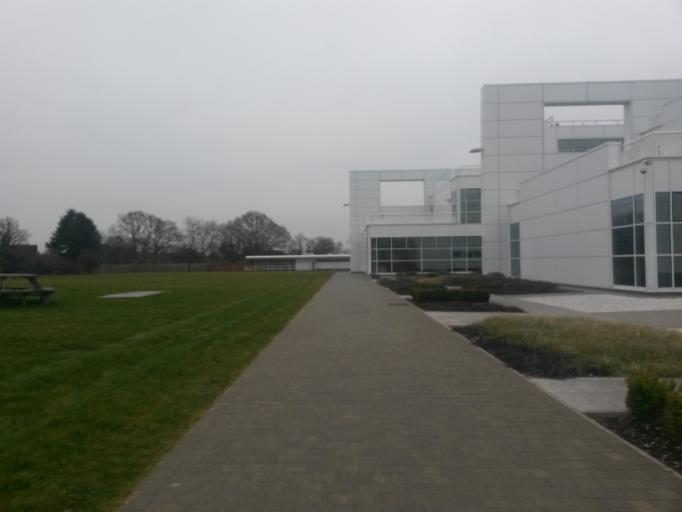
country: GB
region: England
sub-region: Hampshire
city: Totton
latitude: 50.9382
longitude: -1.4696
